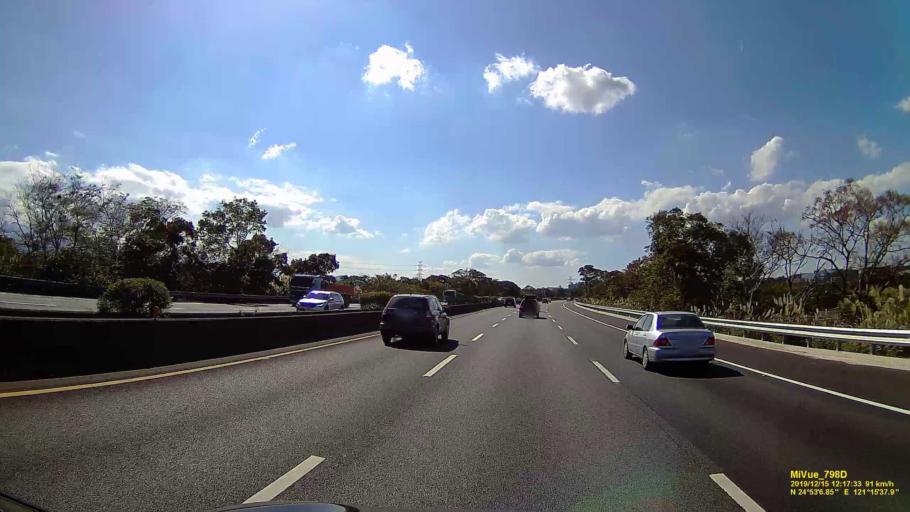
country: TW
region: Taiwan
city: Daxi
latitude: 24.8849
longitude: 121.2599
